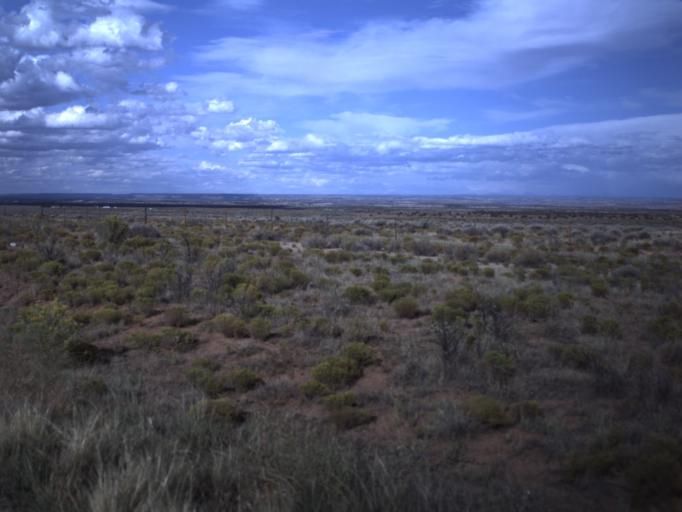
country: US
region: Utah
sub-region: San Juan County
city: Blanding
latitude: 37.3530
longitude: -109.3468
